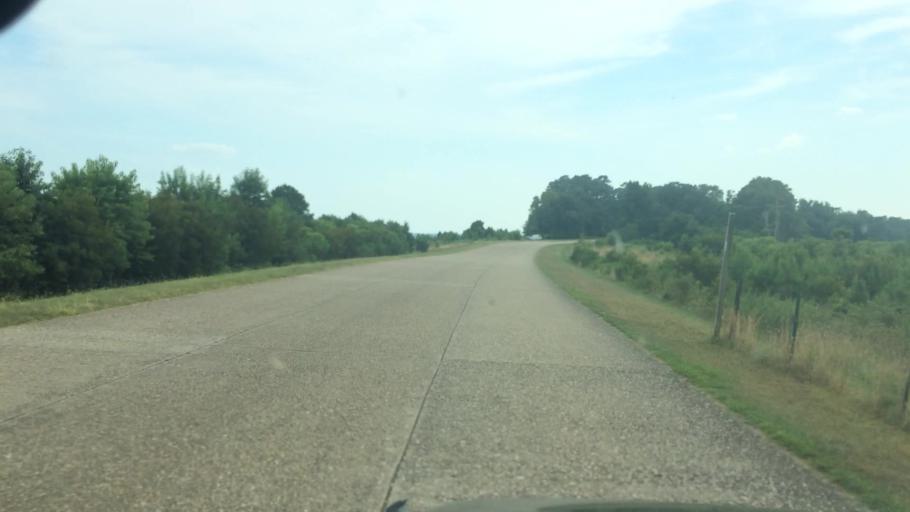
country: US
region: Virginia
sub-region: City of Williamsburg
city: Williamsburg
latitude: 37.2221
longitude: -76.6968
